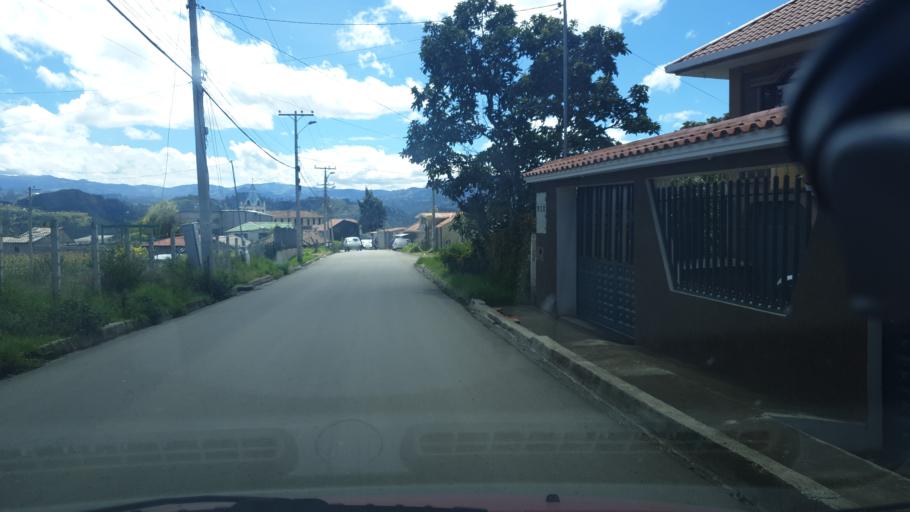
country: EC
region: Azuay
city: Llacao
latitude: -2.8646
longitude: -78.9081
